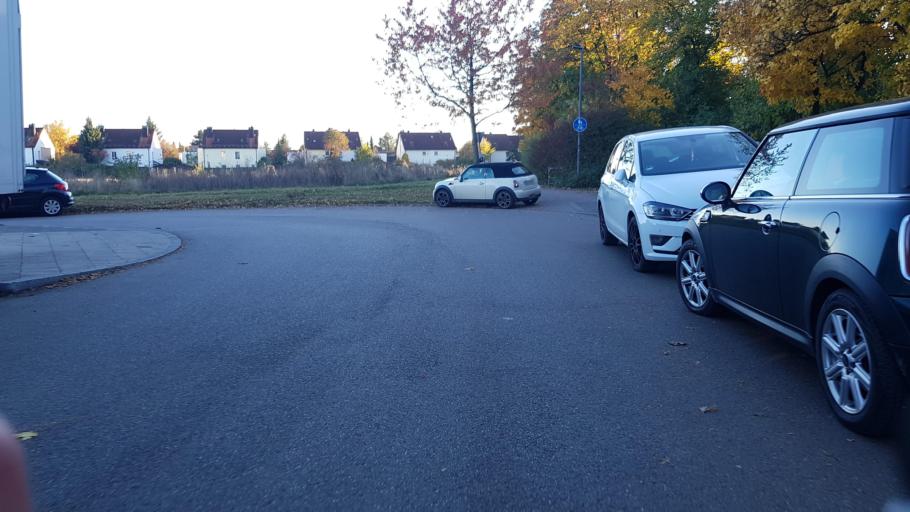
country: DE
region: Bavaria
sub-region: Upper Bavaria
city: Pasing
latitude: 48.1755
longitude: 11.4660
